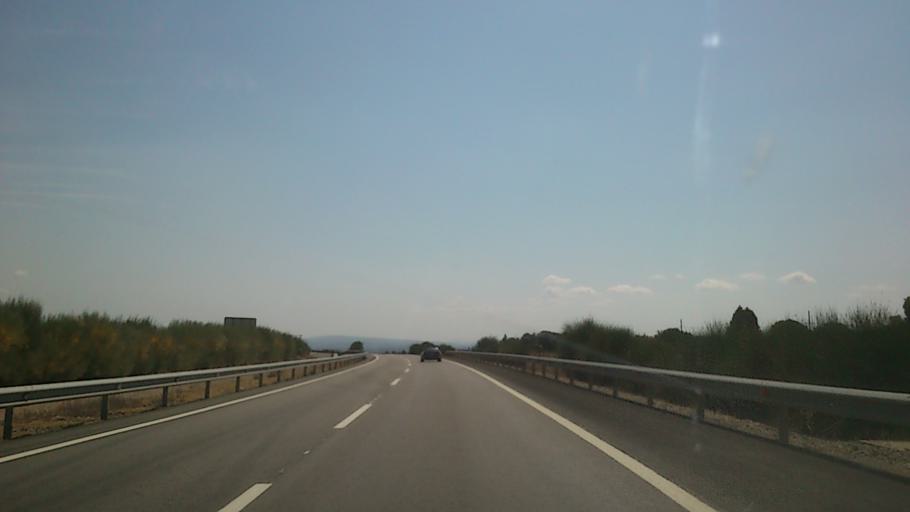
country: ES
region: Aragon
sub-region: Provincia de Teruel
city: Valbona
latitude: 40.1892
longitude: -0.9042
